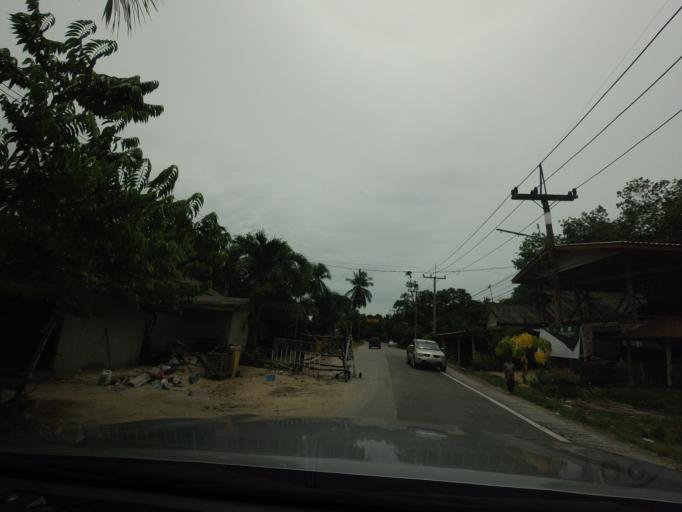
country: TH
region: Pattani
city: Sai Buri
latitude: 6.6482
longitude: 101.5532
